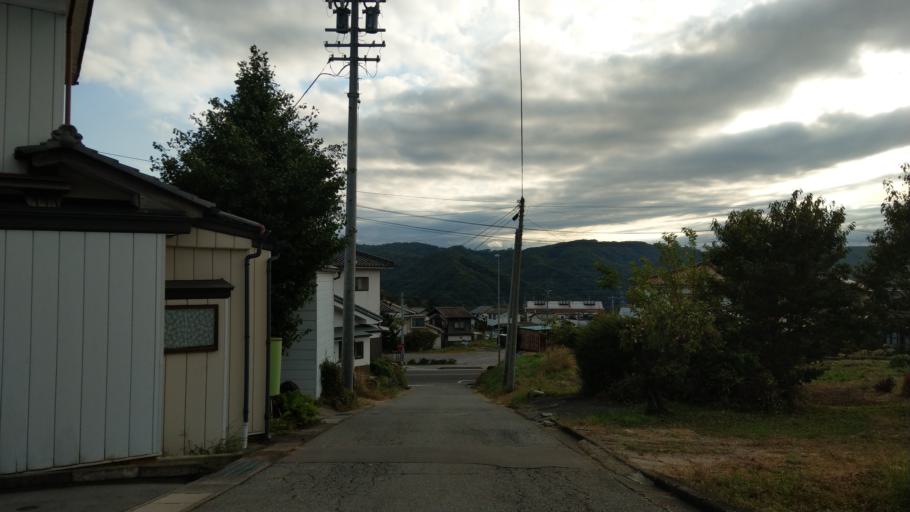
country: JP
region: Nagano
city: Komoro
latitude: 36.3370
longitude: 138.4200
